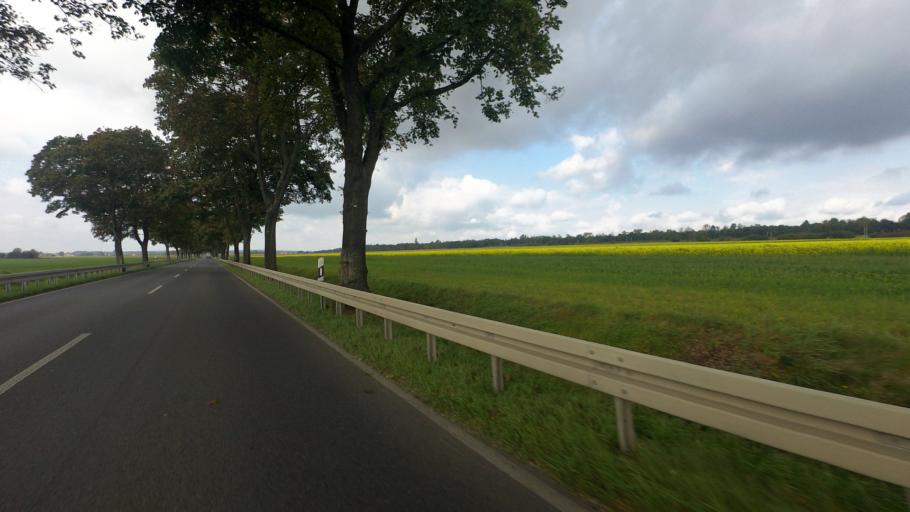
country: DE
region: Brandenburg
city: Plessa
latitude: 51.4671
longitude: 13.5961
